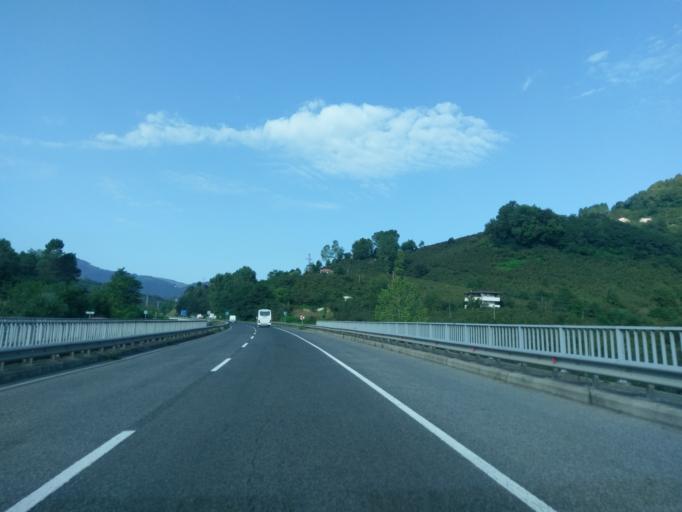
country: TR
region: Ordu
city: Persembe
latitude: 40.9827
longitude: 37.7608
